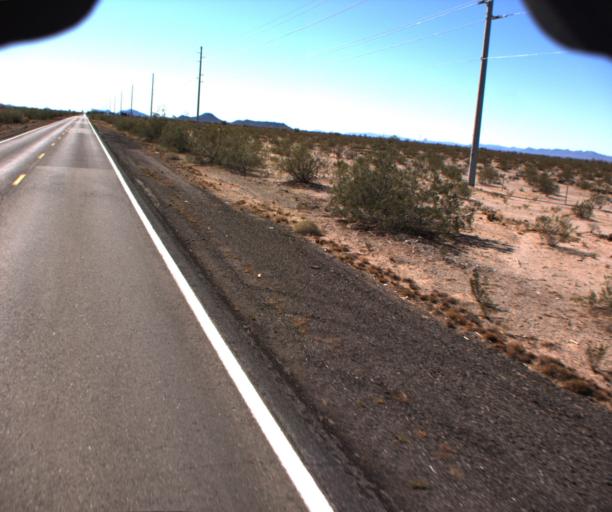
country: US
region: Arizona
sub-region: La Paz County
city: Salome
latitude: 33.8175
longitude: -113.8578
